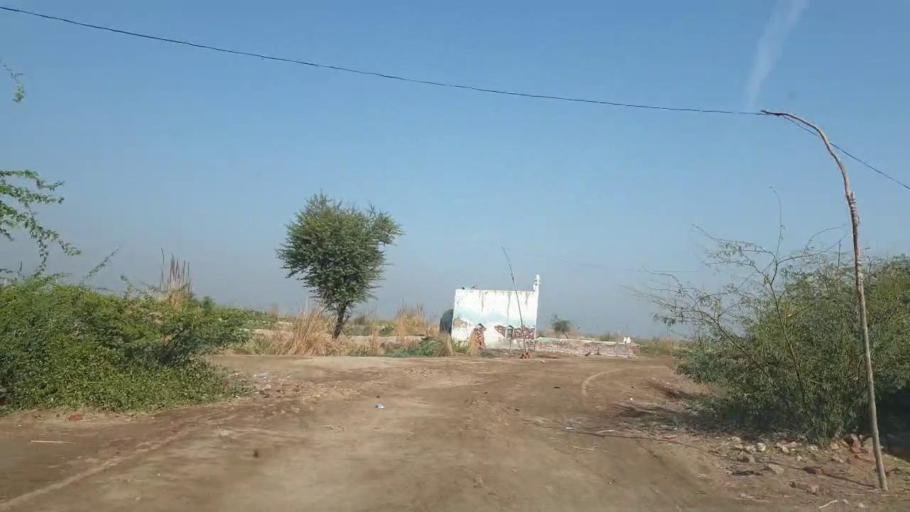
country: PK
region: Sindh
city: Mirpur Khas
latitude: 25.5212
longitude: 69.0669
